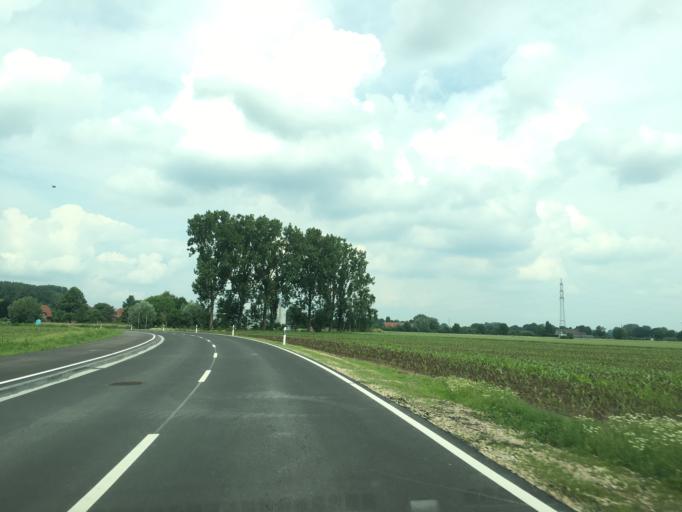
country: DE
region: North Rhine-Westphalia
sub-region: Regierungsbezirk Munster
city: Laer
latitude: 52.0580
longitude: 7.3717
